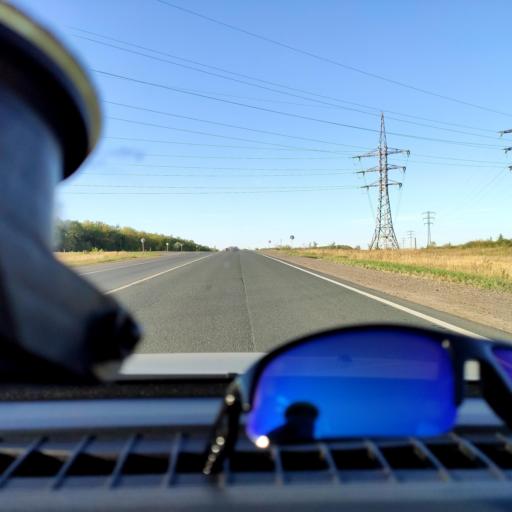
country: RU
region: Samara
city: Chapayevsk
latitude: 52.9470
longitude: 49.7301
